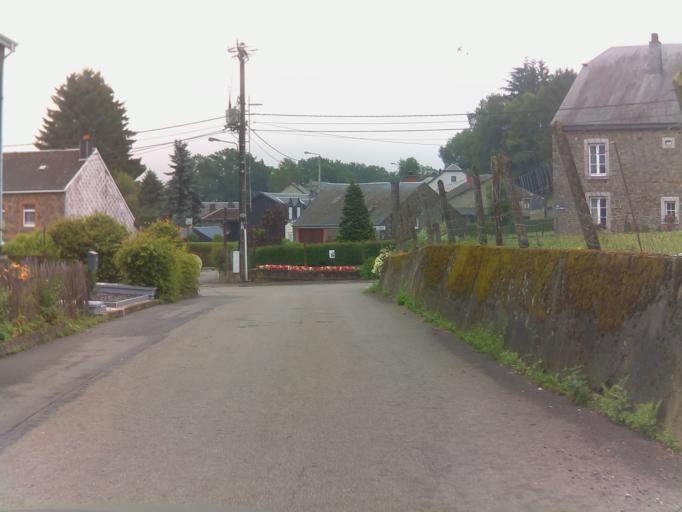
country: BE
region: Wallonia
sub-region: Province du Luxembourg
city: Libin
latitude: 49.9228
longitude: 5.2793
